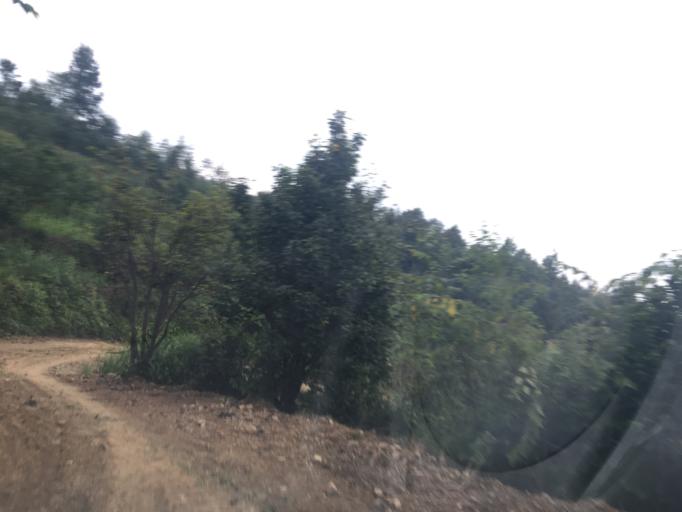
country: CN
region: Guangxi Zhuangzu Zizhiqu
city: Xinzhou
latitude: 25.1639
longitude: 105.6844
